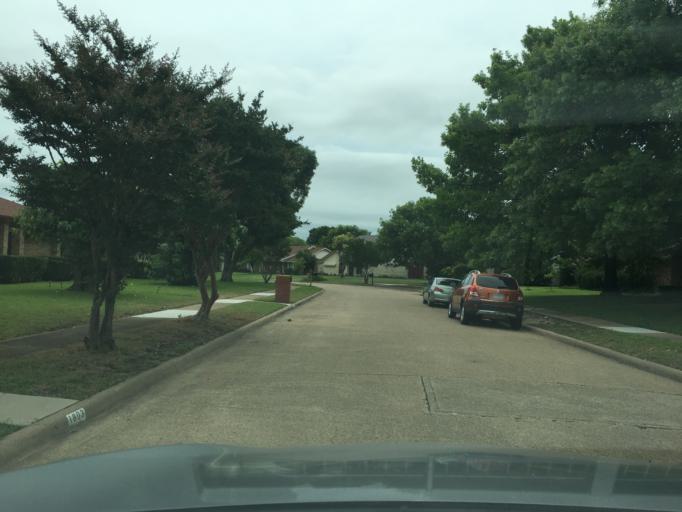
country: US
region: Texas
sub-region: Dallas County
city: Richardson
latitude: 32.9437
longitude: -96.6909
